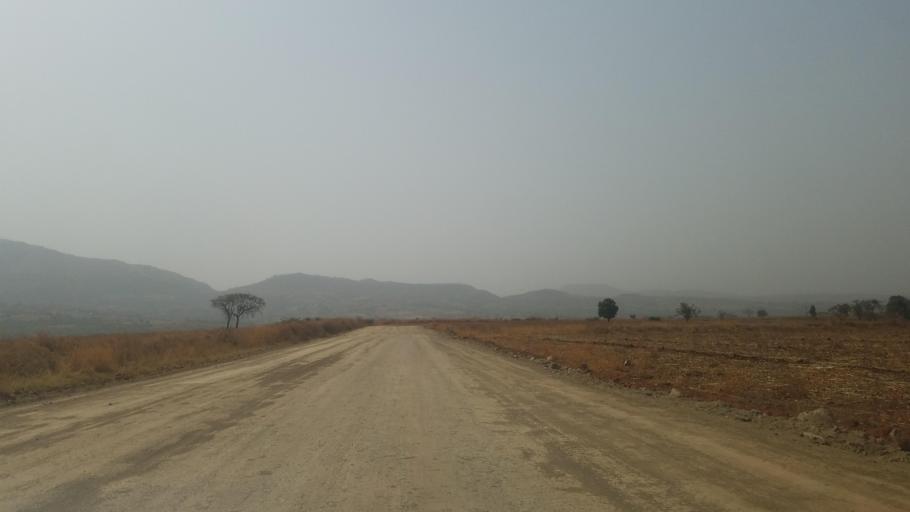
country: ET
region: Amhara
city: Bure
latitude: 10.9018
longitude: 36.4657
